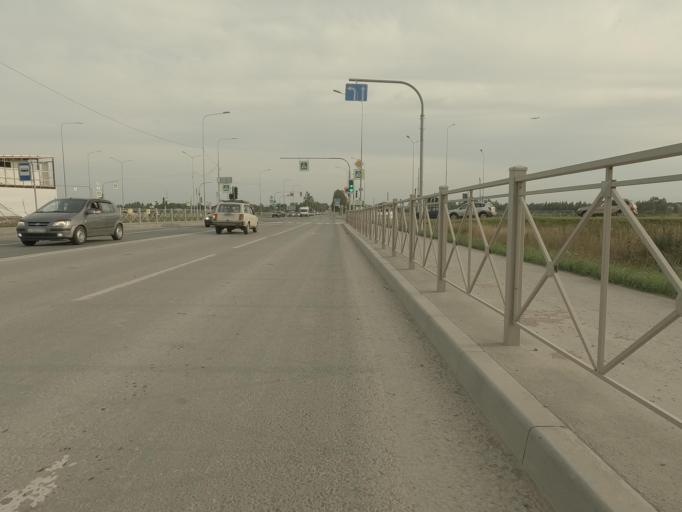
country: RU
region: St.-Petersburg
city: Sosnovaya Polyana
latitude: 59.8415
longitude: 30.0911
